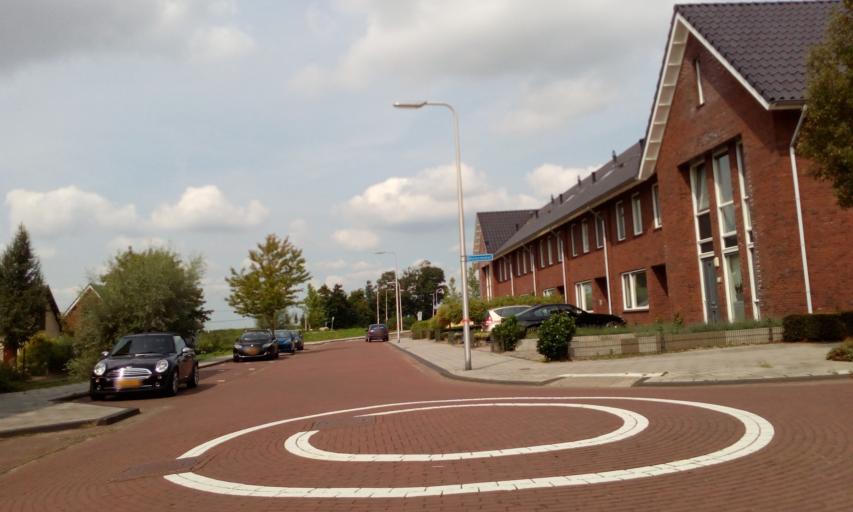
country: NL
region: South Holland
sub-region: Gemeente Lansingerland
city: Bleiswijk
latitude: 52.0176
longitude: 4.5822
